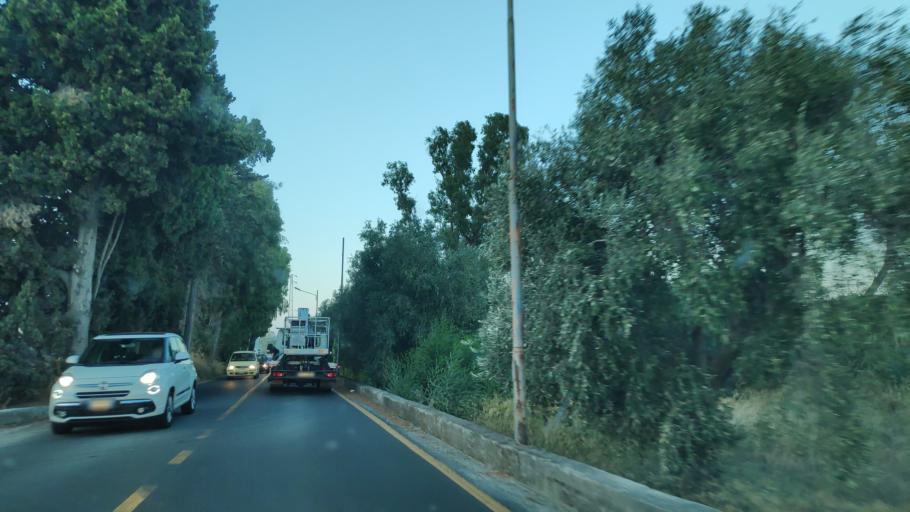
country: IT
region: Calabria
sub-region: Provincia di Reggio Calabria
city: Caulonia Marina
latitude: 38.3470
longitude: 16.4685
